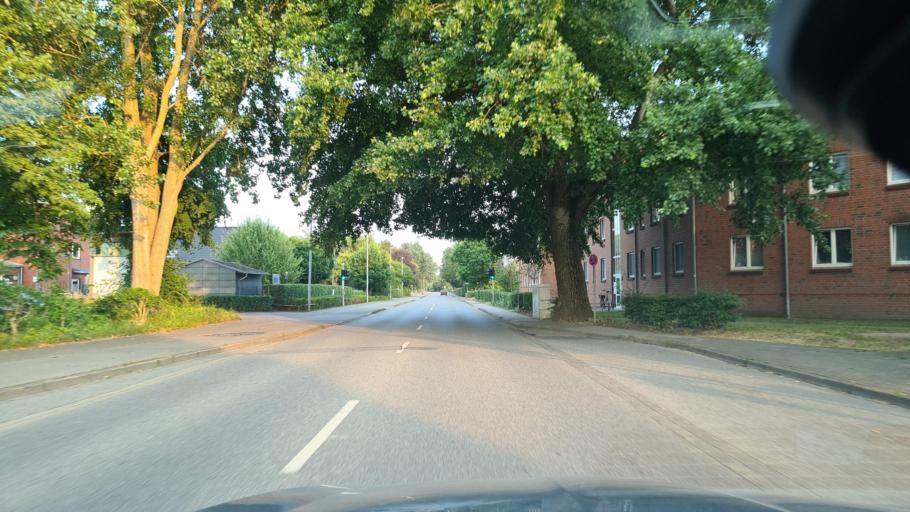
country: DE
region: Schleswig-Holstein
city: Husum
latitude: 54.4919
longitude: 9.0343
